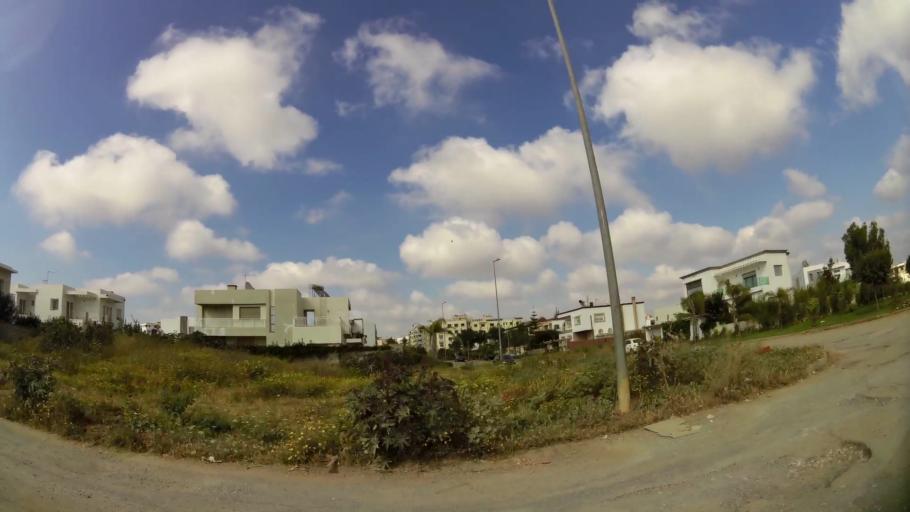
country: MA
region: Rabat-Sale-Zemmour-Zaer
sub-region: Skhirate-Temara
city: Temara
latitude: 33.9515
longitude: -6.8771
